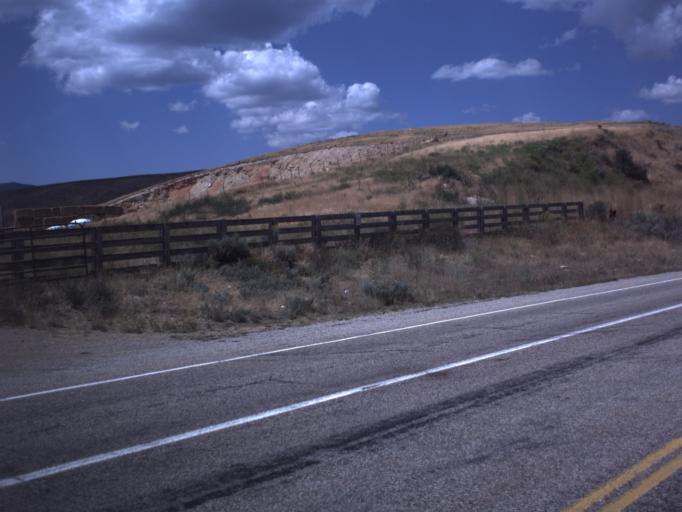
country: US
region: Utah
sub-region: Rich County
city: Randolph
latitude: 41.8464
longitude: -111.3514
